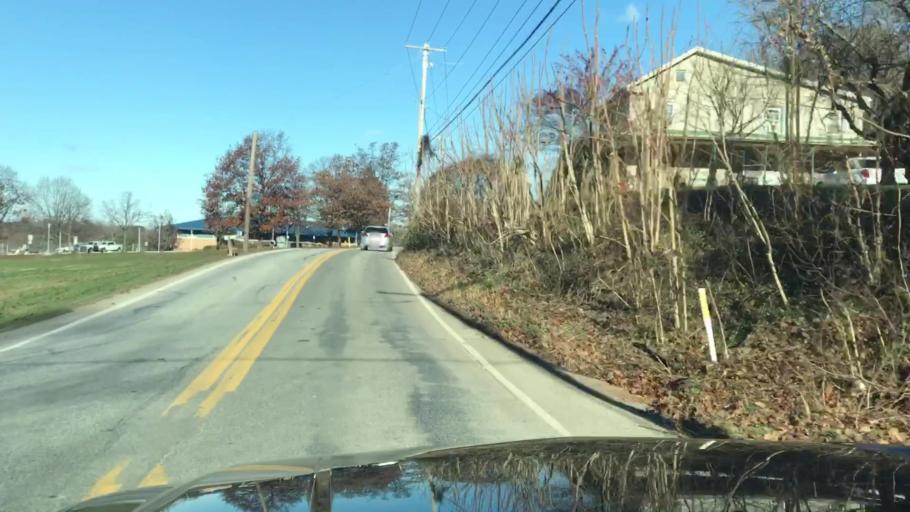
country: US
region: Pennsylvania
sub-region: Cumberland County
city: Lower Allen
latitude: 40.1884
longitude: -76.8896
